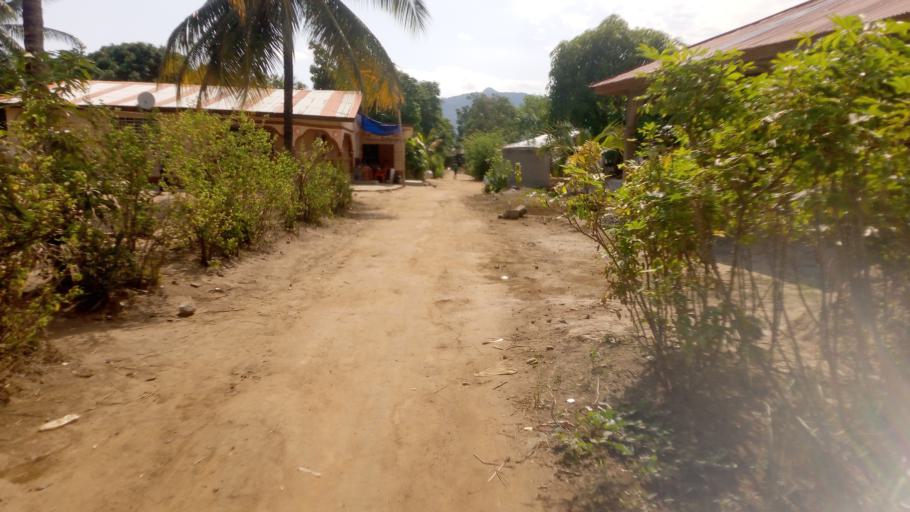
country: SL
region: Western Area
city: Waterloo
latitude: 8.3202
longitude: -13.0740
